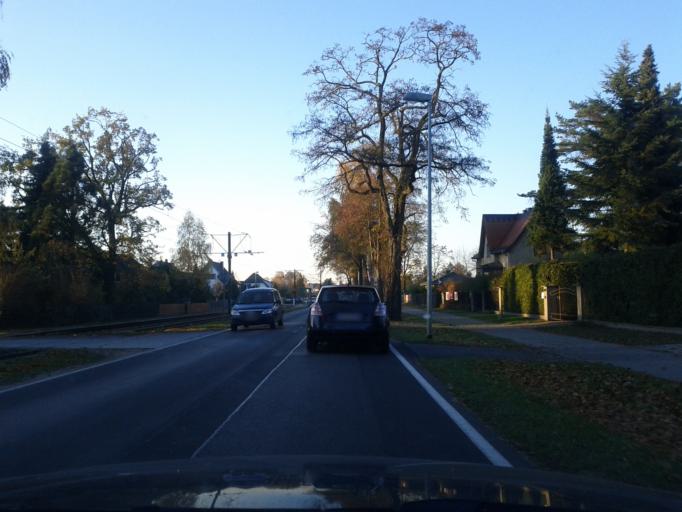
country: DE
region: Brandenburg
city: Schoneiche
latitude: 52.4762
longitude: 13.7106
